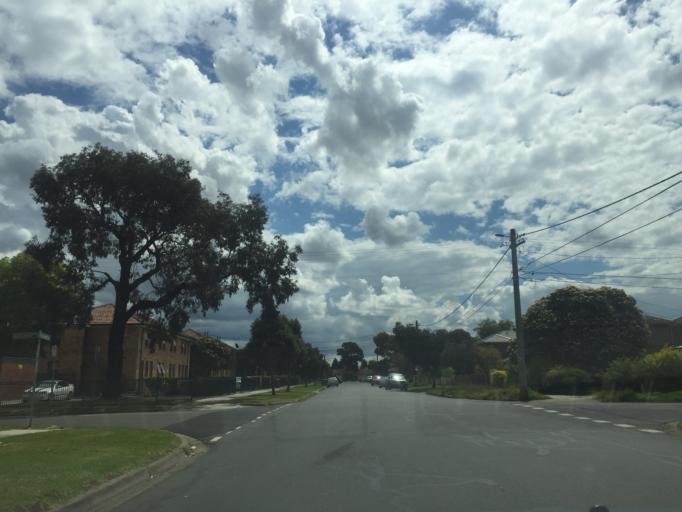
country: AU
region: Victoria
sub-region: Darebin
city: Reservoir
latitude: -37.7130
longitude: 145.0165
